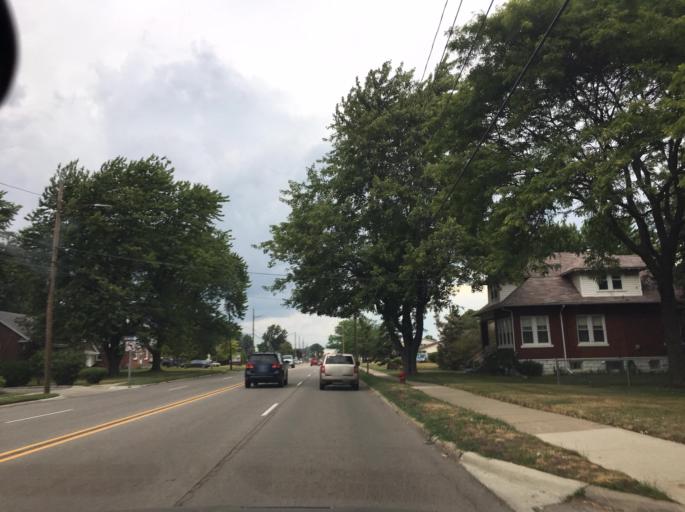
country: US
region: Michigan
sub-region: Macomb County
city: Fraser
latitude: 42.5202
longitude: -82.9420
